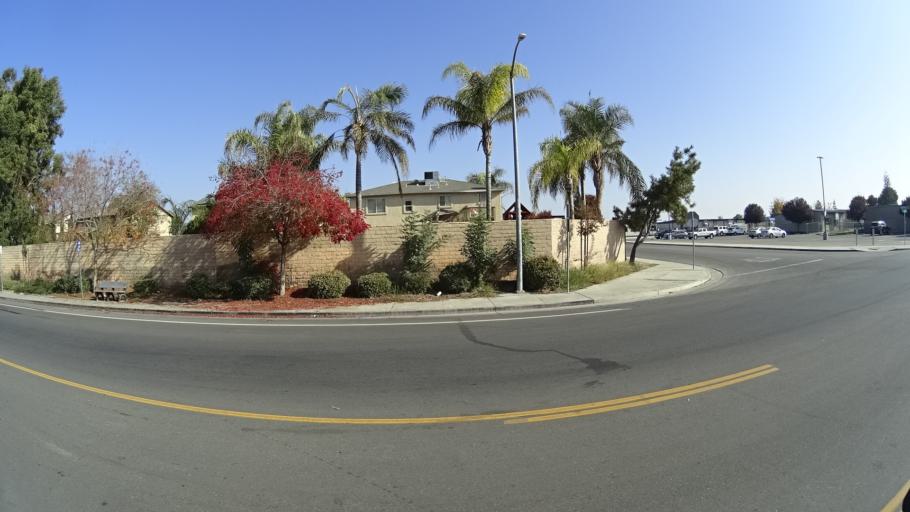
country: US
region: California
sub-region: Kern County
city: Greenfield
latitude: 35.3071
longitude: -119.0119
